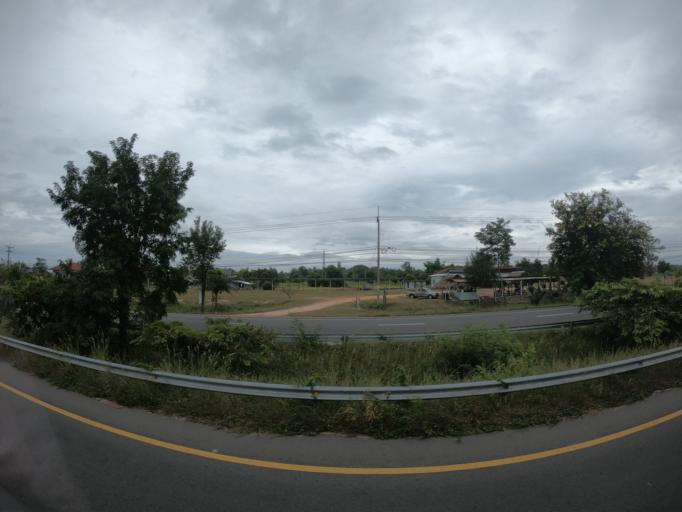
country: TH
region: Roi Et
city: Changhan
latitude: 16.1153
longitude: 103.4960
